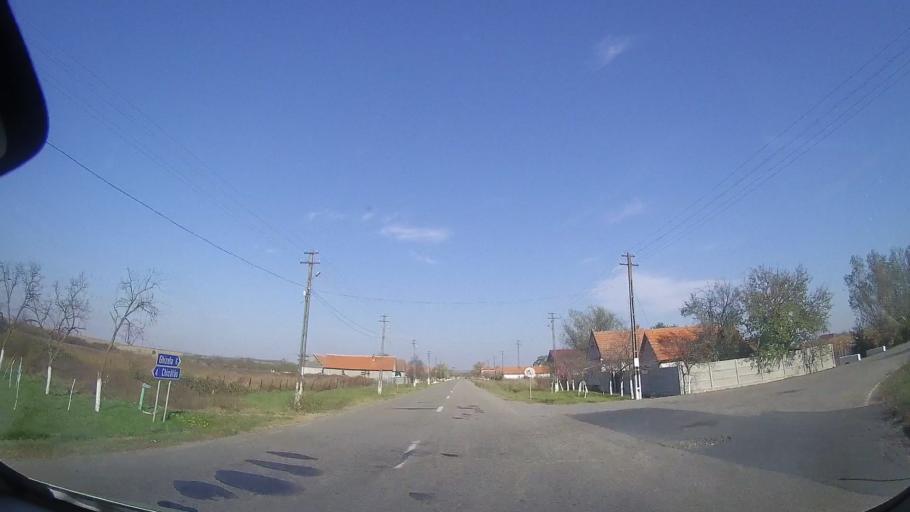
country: RO
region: Timis
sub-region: Comuna Ghizela
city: Ghizela
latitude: 45.7906
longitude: 21.7301
